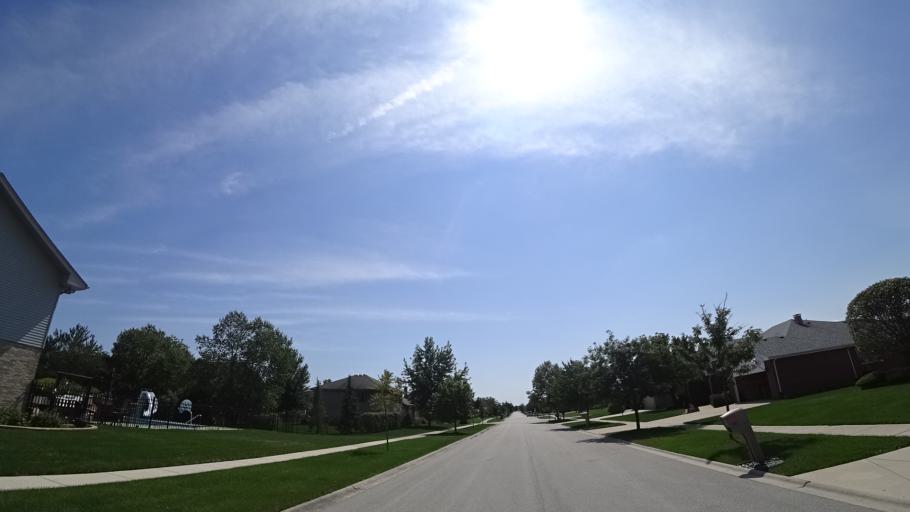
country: US
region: Illinois
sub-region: Cook County
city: Orland Hills
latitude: 41.5710
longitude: -87.8340
